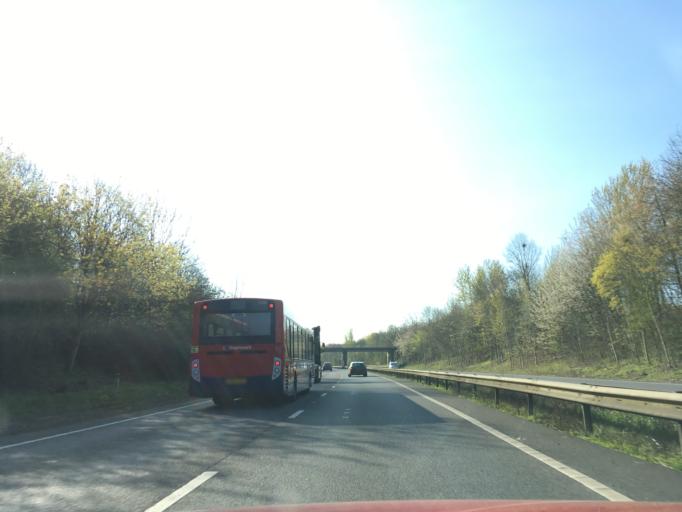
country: GB
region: England
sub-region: Milton Keynes
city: Stony Stratford
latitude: 52.0564
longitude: -0.8381
